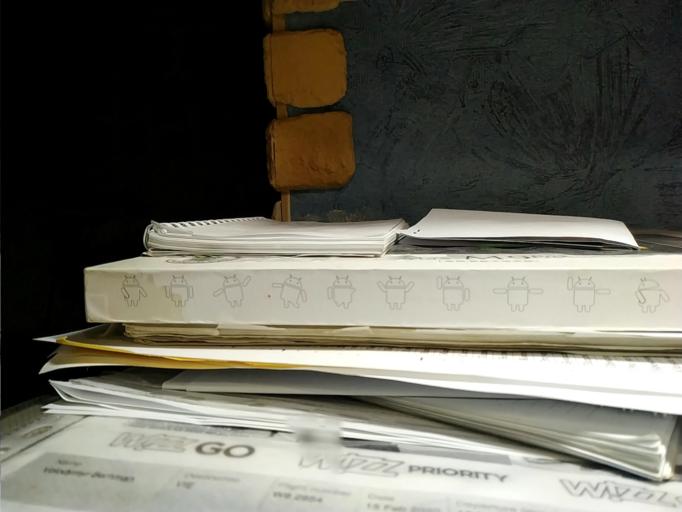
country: RU
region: Arkhangelskaya
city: Konevo
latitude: 62.7393
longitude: 38.5936
